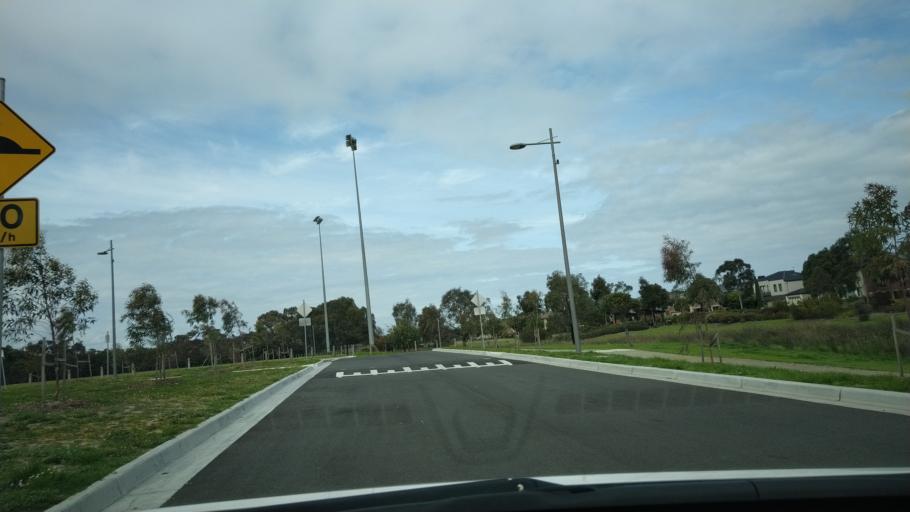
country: AU
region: Victoria
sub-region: Greater Dandenong
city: Keysborough
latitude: -37.9971
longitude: 145.1530
